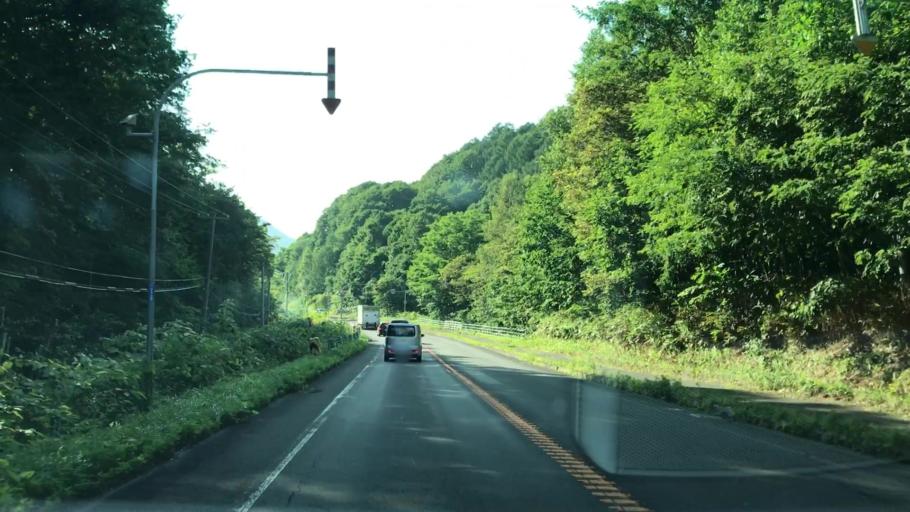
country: JP
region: Hokkaido
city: Iwamizawa
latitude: 42.9363
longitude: 142.0510
